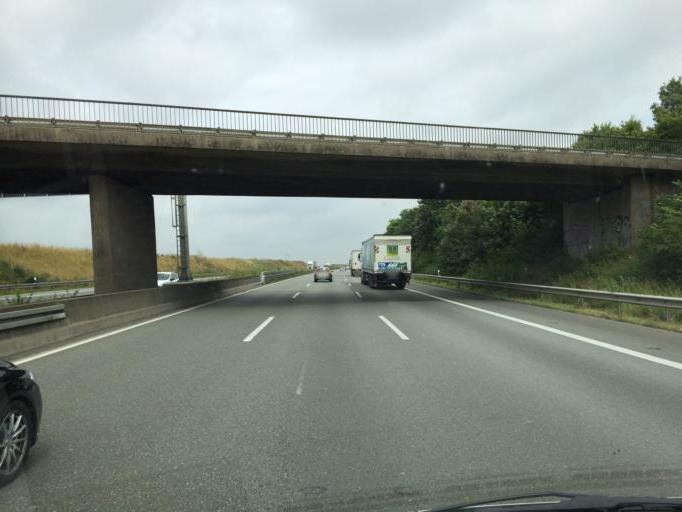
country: DE
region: North Rhine-Westphalia
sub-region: Regierungsbezirk Detmold
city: Herford
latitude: 52.0655
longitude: 8.6617
